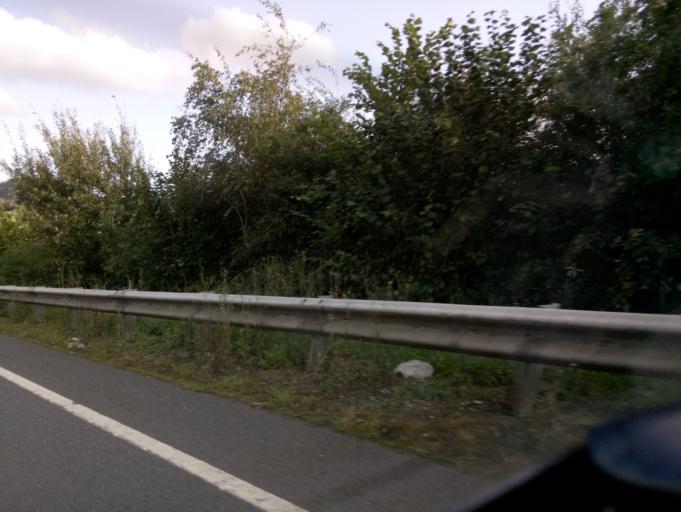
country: GB
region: Wales
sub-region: Rhondda Cynon Taf
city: Llantwit Fardre
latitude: 51.5458
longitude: -3.3417
